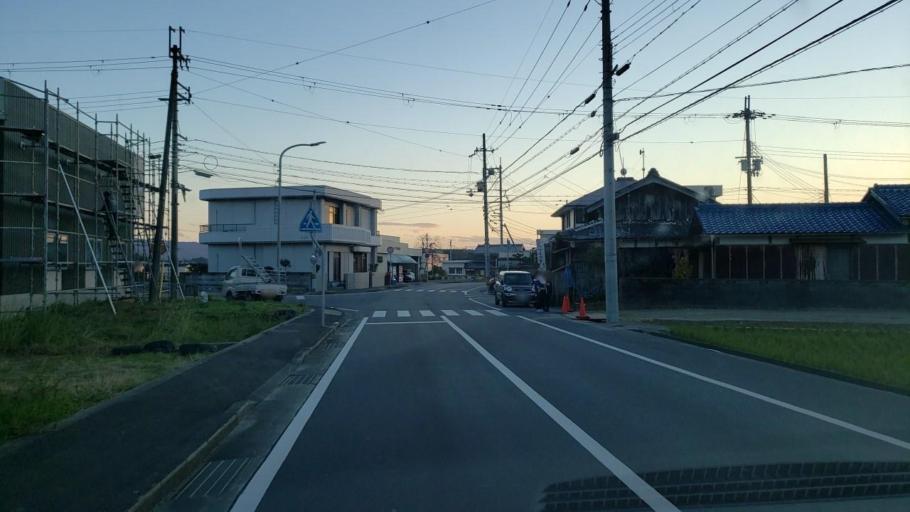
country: JP
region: Hyogo
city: Fukura
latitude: 34.3360
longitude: 134.7793
